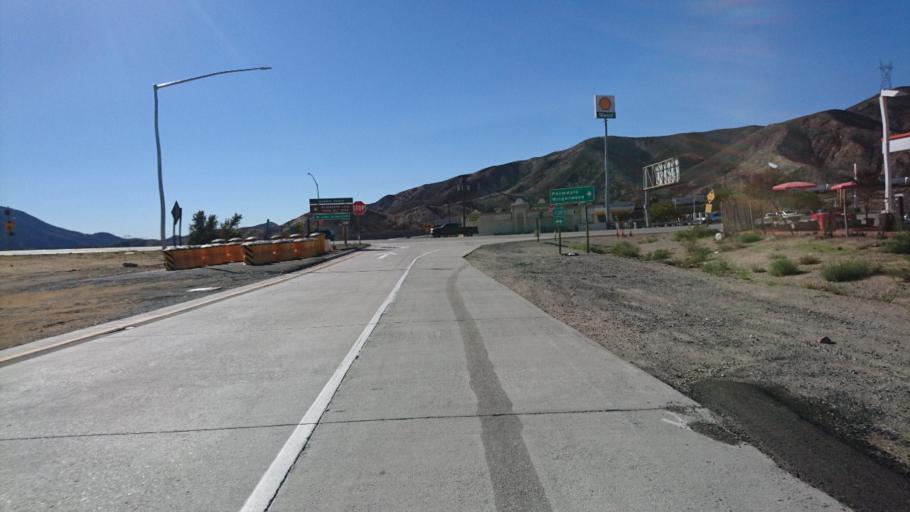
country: US
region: California
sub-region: San Bernardino County
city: Oak Hills
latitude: 34.3124
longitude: -117.4775
